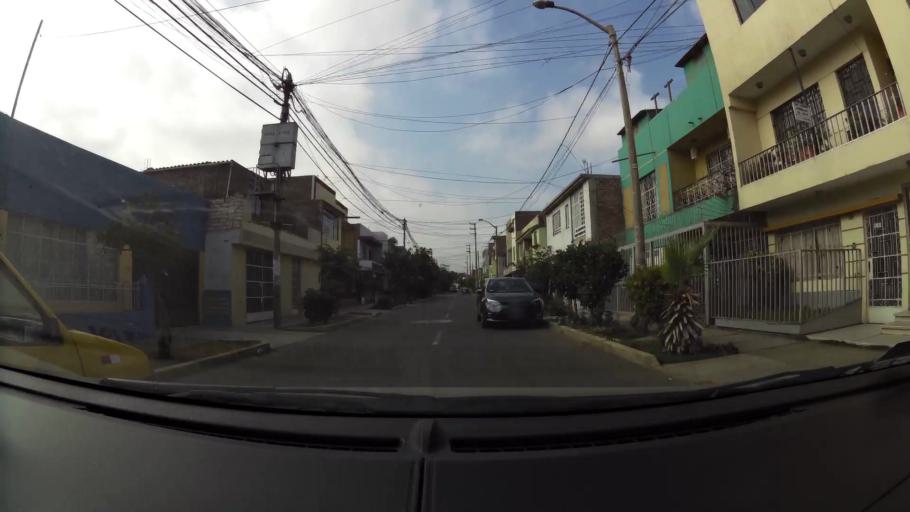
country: PE
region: La Libertad
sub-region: Provincia de Trujillo
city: Trujillo
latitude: -8.1099
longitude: -79.0133
